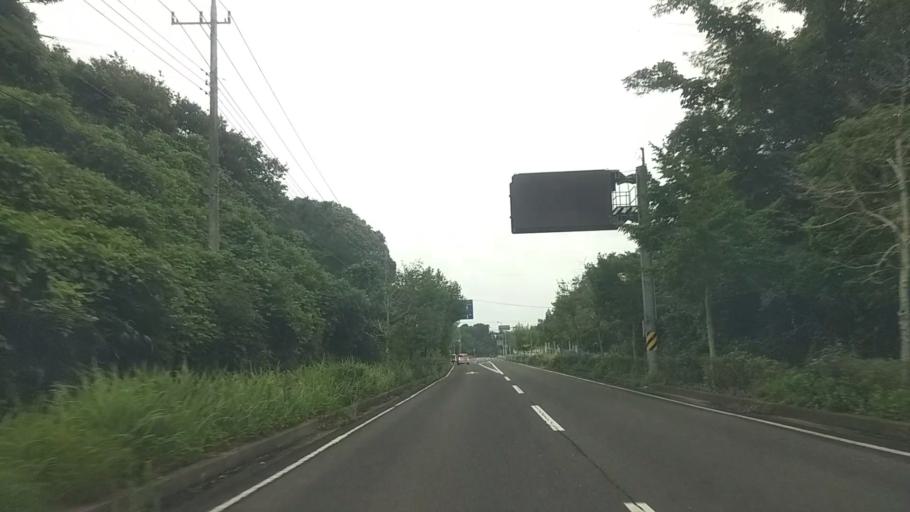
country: JP
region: Chiba
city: Kisarazu
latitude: 35.3858
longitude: 140.0028
